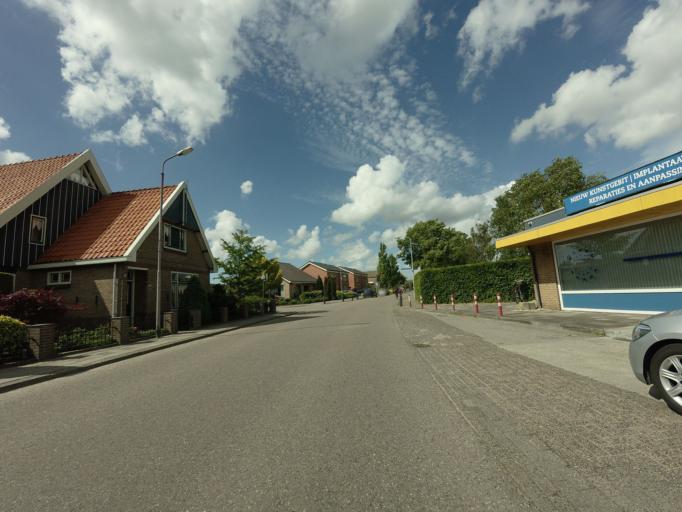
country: NL
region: North Holland
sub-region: Gemeente Hoorn
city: Hoorn
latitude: 52.6923
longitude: 5.0566
